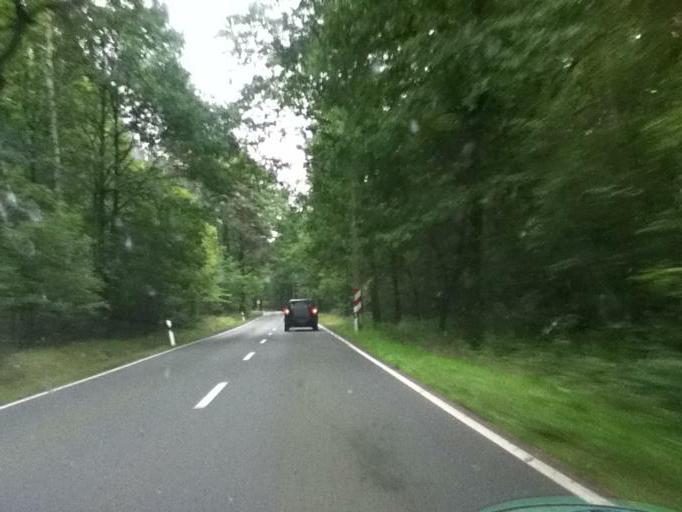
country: DE
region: Saxony
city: Albertstadt
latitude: 51.1027
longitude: 13.7661
